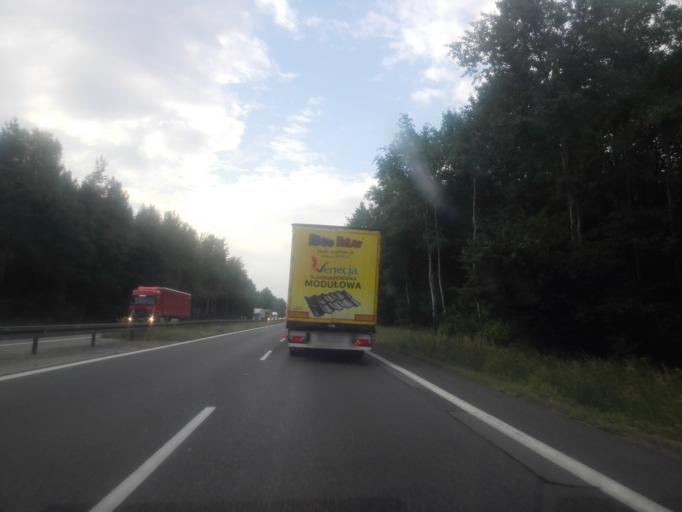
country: PL
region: Silesian Voivodeship
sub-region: Powiat bedzinski
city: Siewierz
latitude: 50.5204
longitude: 19.1934
